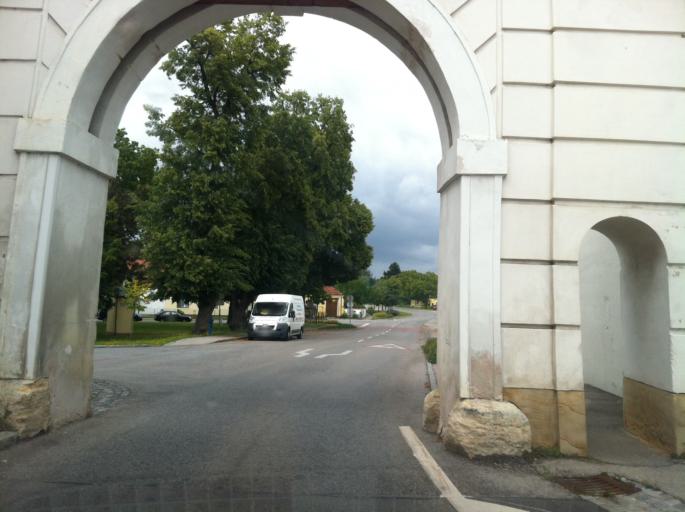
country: AT
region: Lower Austria
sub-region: Politischer Bezirk Tulln
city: Langenrohr
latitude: 48.2844
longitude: 16.0100
